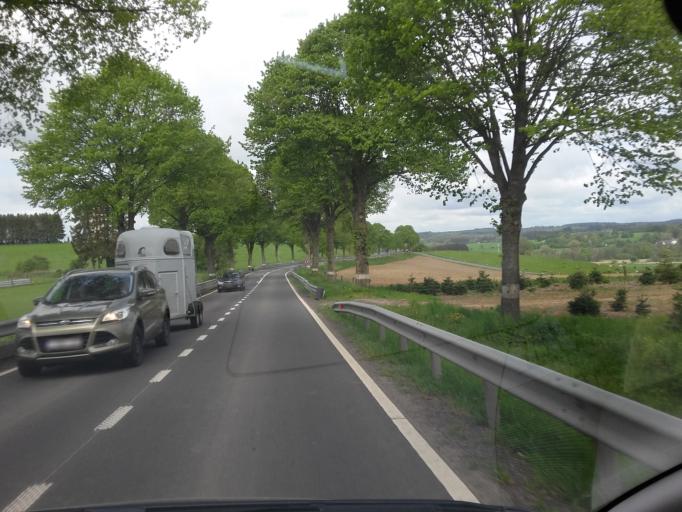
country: BE
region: Wallonia
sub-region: Province du Luxembourg
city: Neufchateau
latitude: 49.8443
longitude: 5.3887
